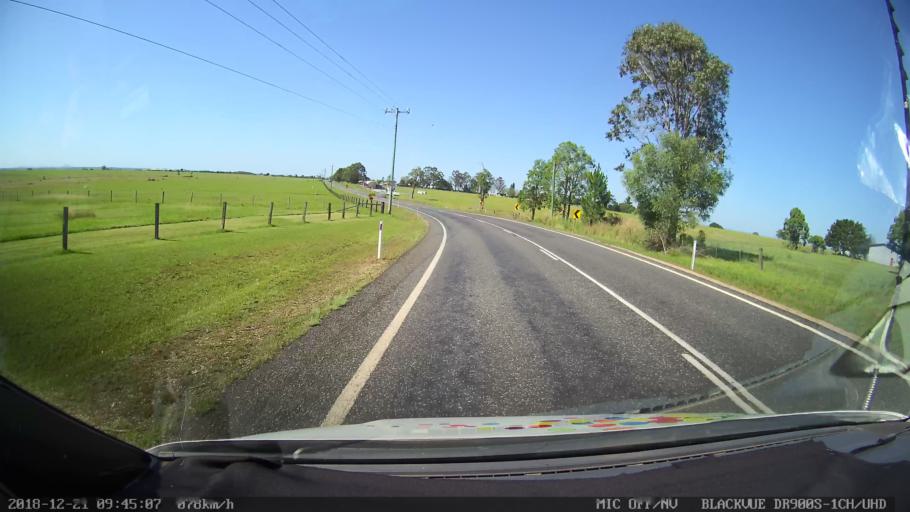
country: AU
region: New South Wales
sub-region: Clarence Valley
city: Grafton
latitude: -29.6249
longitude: 152.9293
